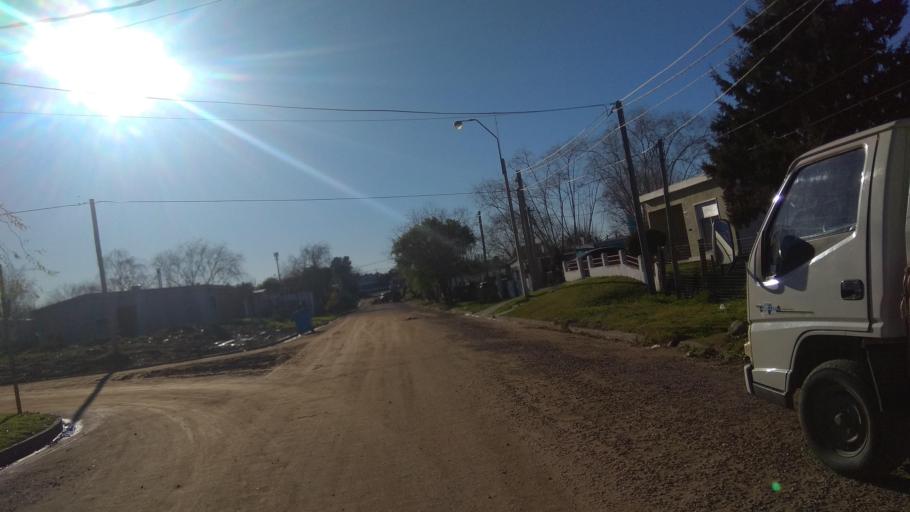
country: UY
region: Florida
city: Florida
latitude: -34.0985
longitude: -56.2373
